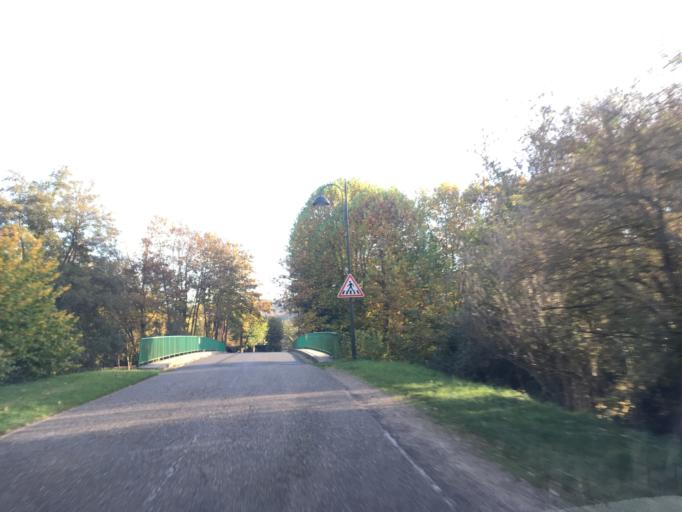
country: FR
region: Haute-Normandie
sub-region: Departement de l'Eure
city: Heudreville-sur-Eure
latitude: 49.1035
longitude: 1.2409
